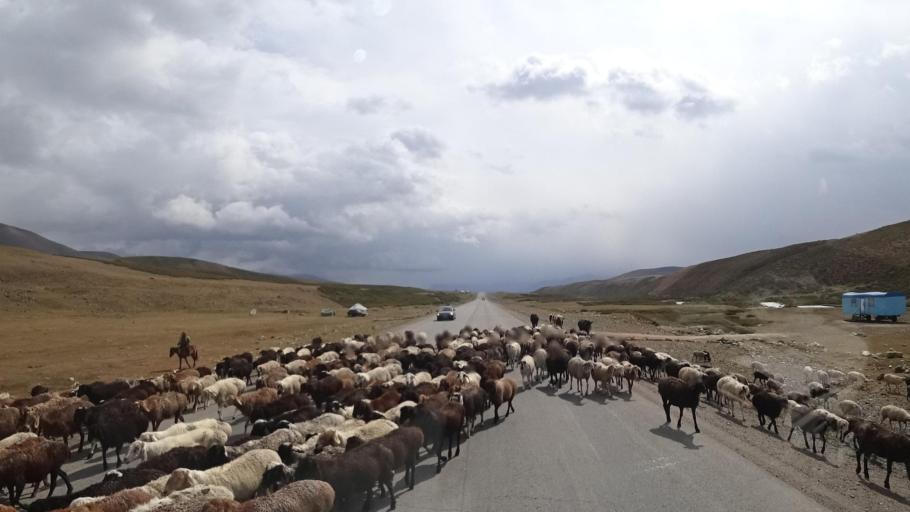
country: KG
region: Jalal-Abad
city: Uch-Terek
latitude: 42.2064
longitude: 73.2721
